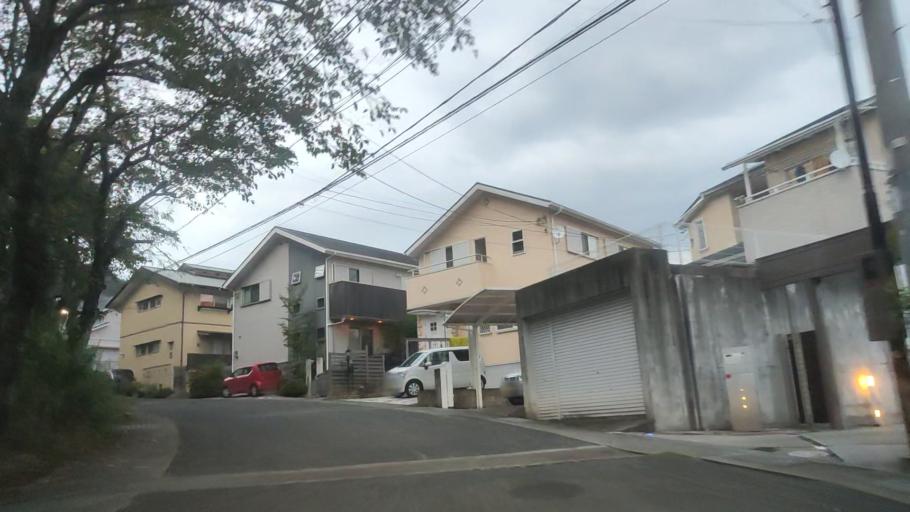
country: JP
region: Wakayama
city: Hashimoto
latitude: 34.3682
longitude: 135.6041
